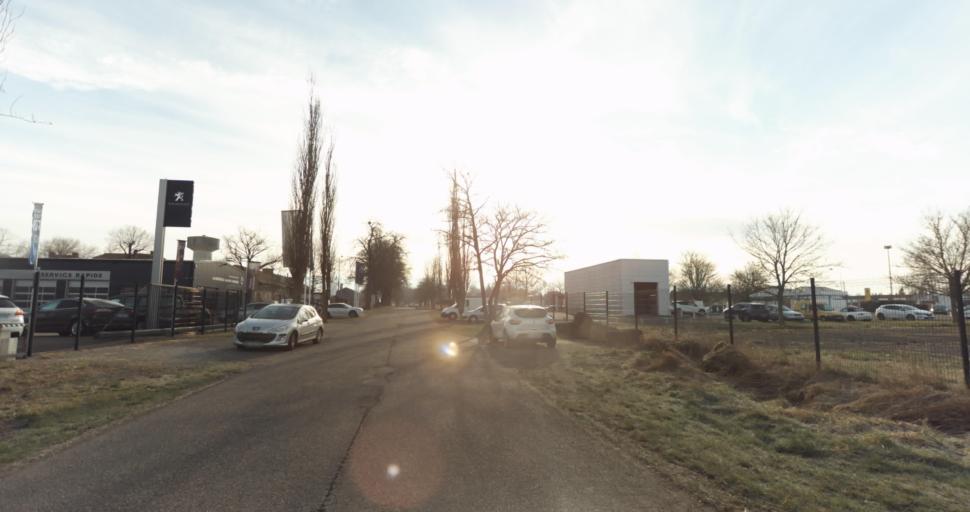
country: FR
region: Lorraine
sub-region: Departement de Meurthe-et-Moselle
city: Jarny
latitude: 49.1555
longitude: 5.8916
